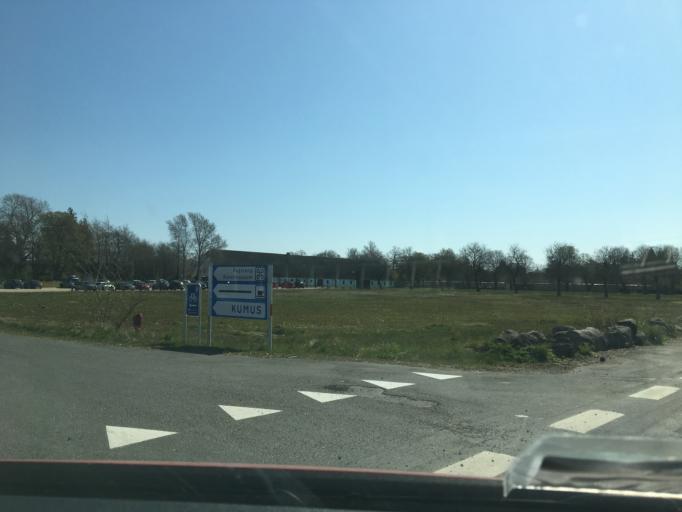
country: DK
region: Zealand
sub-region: Guldborgsund Kommune
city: Nykobing Falster
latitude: 54.7251
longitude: 11.7955
